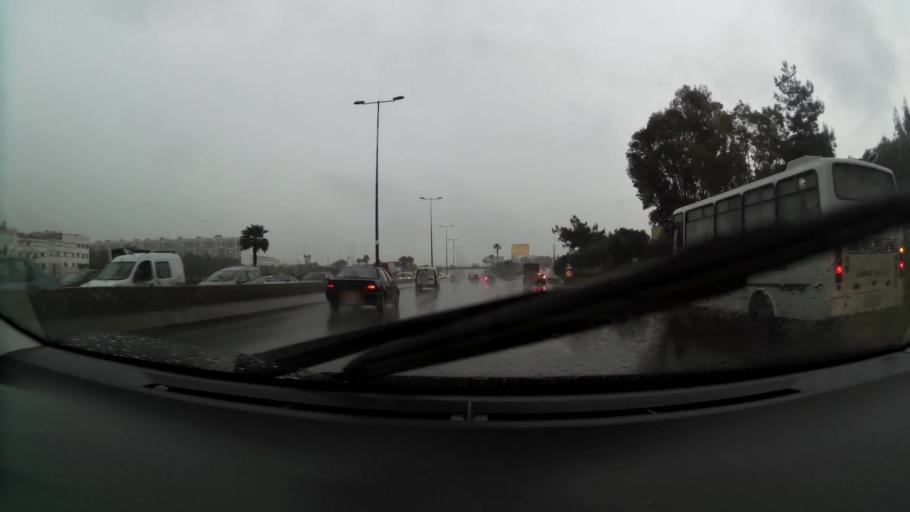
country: MA
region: Grand Casablanca
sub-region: Casablanca
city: Casablanca
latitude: 33.5753
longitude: -7.5617
